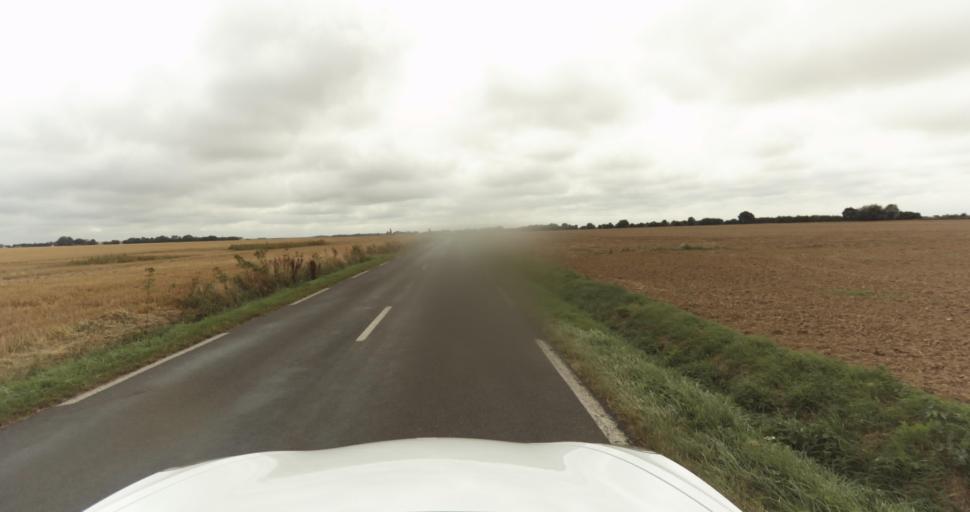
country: FR
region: Haute-Normandie
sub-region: Departement de l'Eure
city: Claville
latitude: 49.0823
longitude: 1.0536
